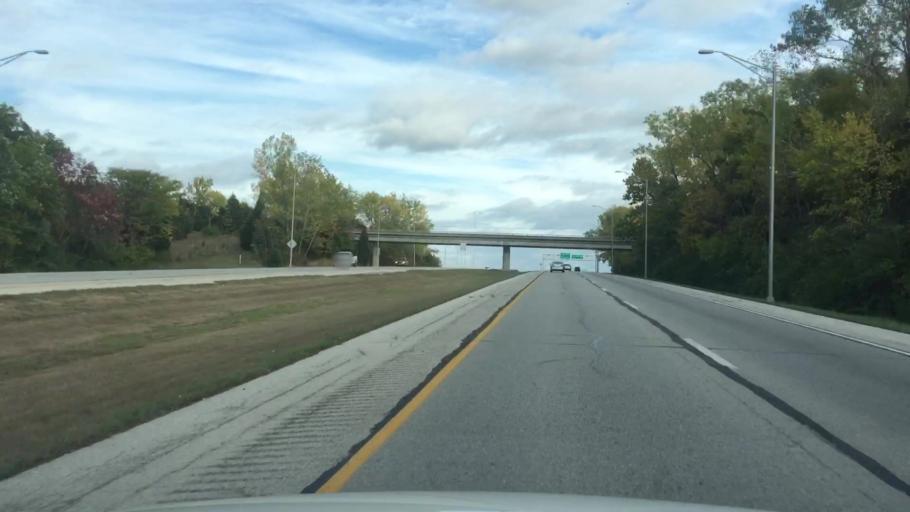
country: US
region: Kansas
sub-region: Wyandotte County
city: Edwardsville
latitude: 39.0104
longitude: -94.7947
